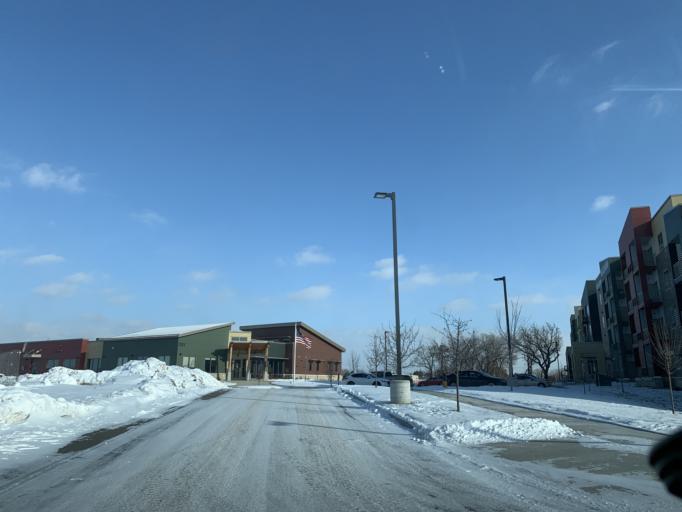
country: US
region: Minnesota
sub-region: Scott County
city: Prior Lake
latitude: 44.7805
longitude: -93.4095
